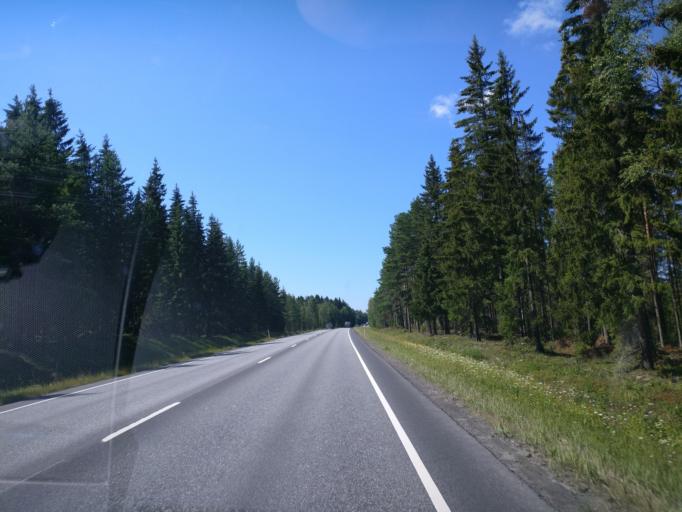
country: FI
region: Satakunta
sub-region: Pori
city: Nakkila
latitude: 61.4574
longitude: 22.0434
